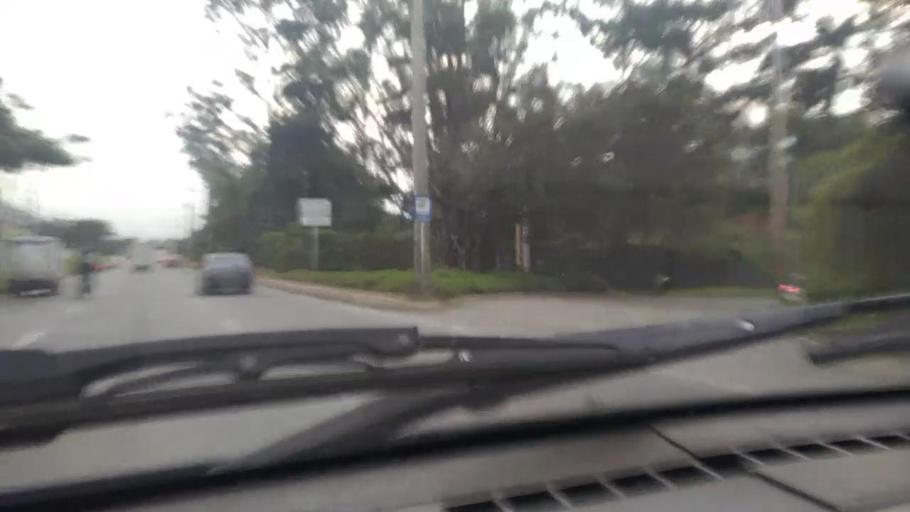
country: CO
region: Antioquia
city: Sabaneta
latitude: 6.1542
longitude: -75.6234
